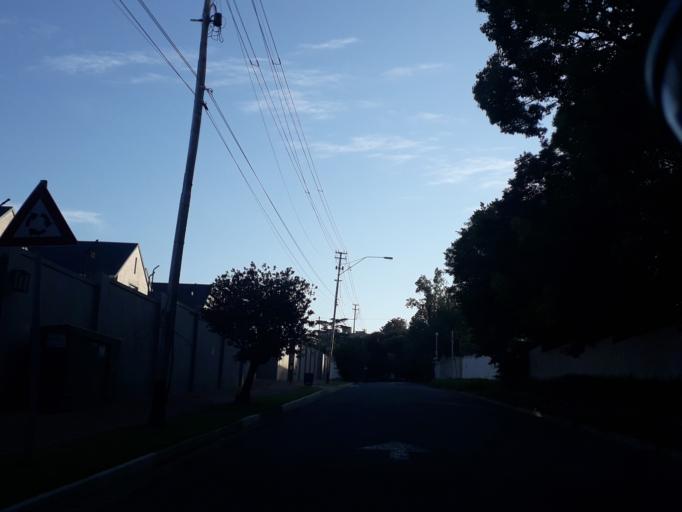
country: ZA
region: Gauteng
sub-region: City of Johannesburg Metropolitan Municipality
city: Johannesburg
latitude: -26.1131
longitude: 28.0283
